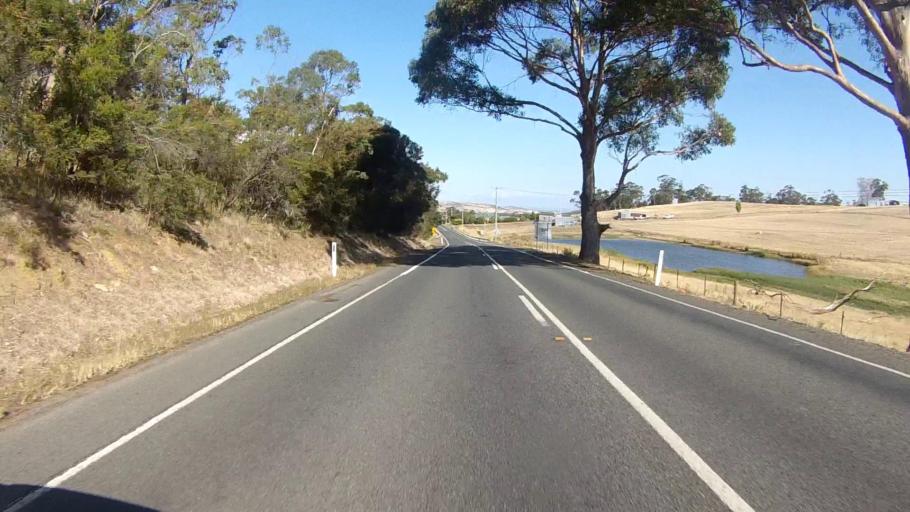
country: AU
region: Tasmania
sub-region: Sorell
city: Sorell
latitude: -42.7105
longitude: 147.5110
